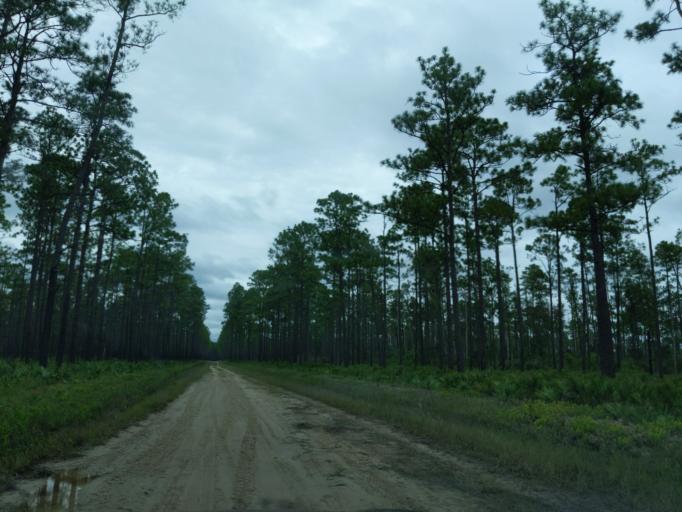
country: US
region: Florida
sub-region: Gadsden County
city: Midway
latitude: 30.3707
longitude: -84.4861
